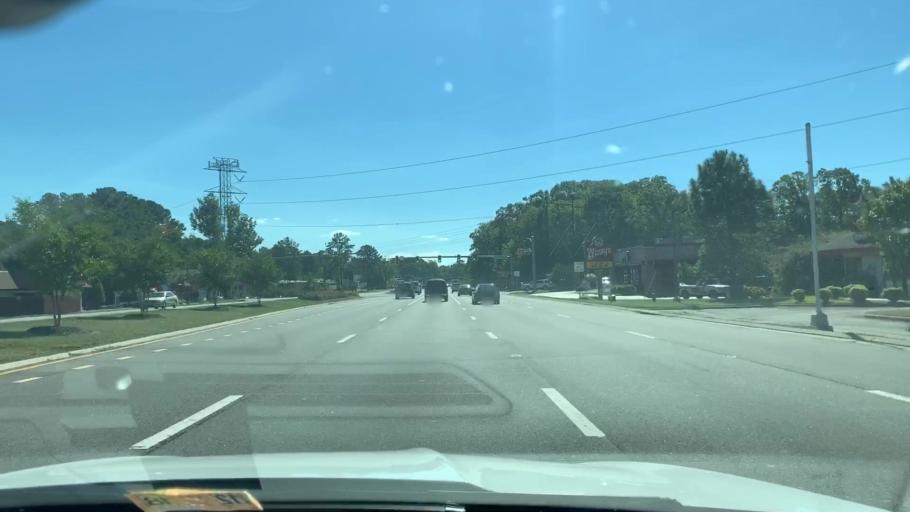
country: US
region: Virginia
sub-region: York County
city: Yorktown
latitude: 37.1463
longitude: -76.4587
